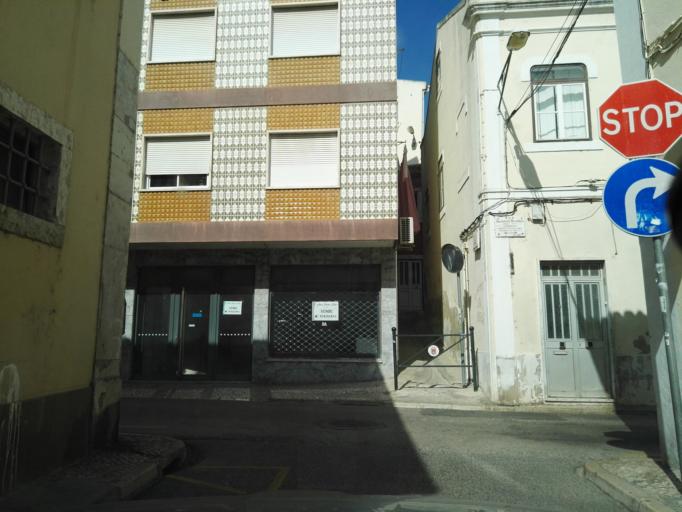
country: PT
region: Lisbon
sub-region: Vila Franca de Xira
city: Alhandra
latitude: 38.9279
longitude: -9.0079
